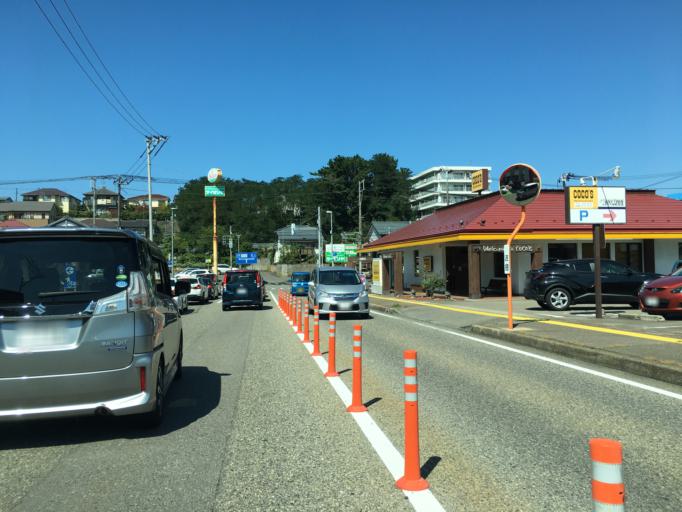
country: JP
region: Niigata
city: Niigata-shi
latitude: 37.8970
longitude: 139.0058
